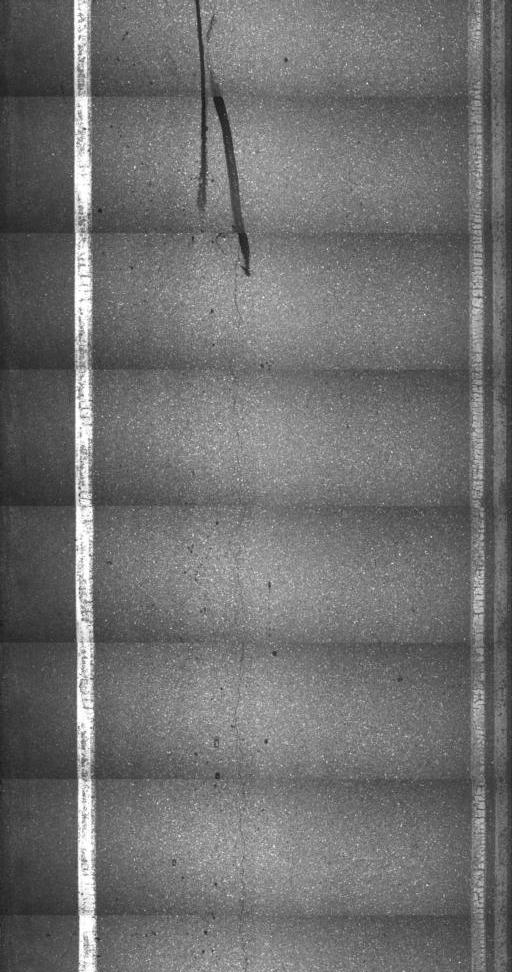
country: US
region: Vermont
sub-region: Orleans County
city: Newport
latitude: 44.9757
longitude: -72.4138
